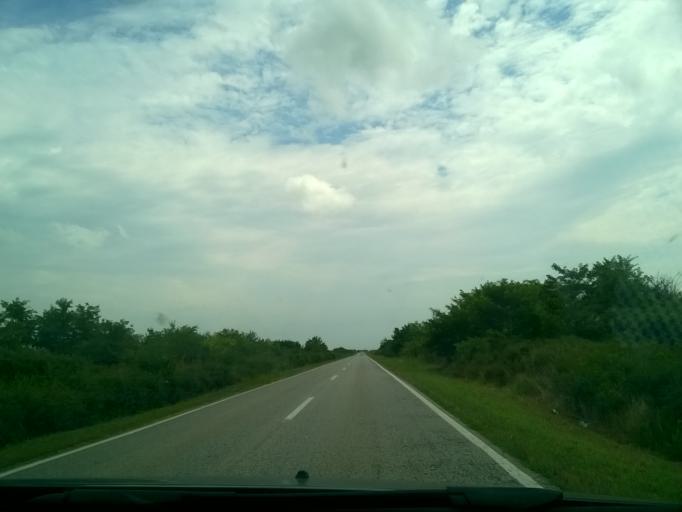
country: RS
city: Lazarevo
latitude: 45.3884
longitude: 20.6016
